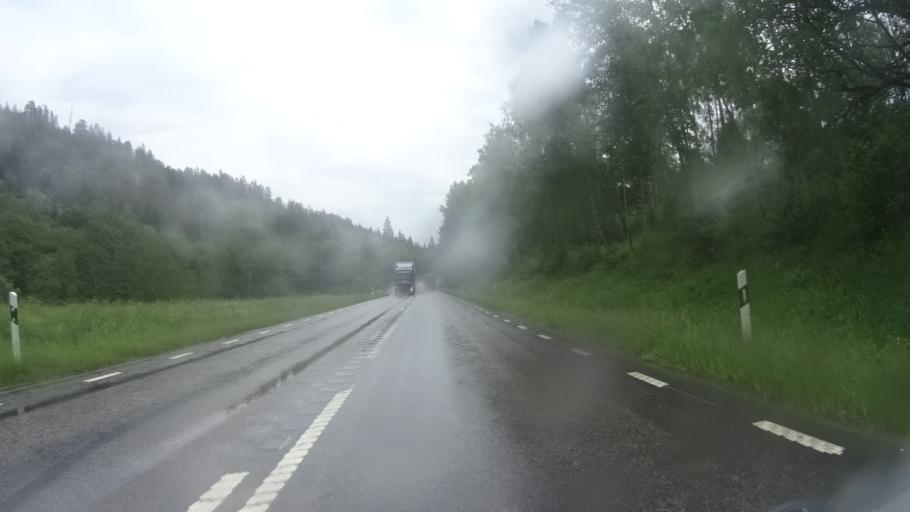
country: SE
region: OEstergoetland
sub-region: Kinda Kommun
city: Kisa
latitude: 57.9716
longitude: 15.6482
